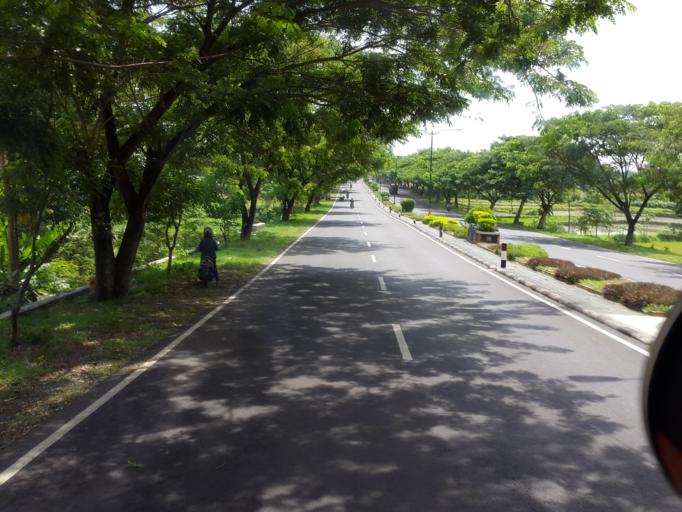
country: ID
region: West Nusa Tenggara
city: Karang Kuripan
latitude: -8.6674
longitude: 116.1622
